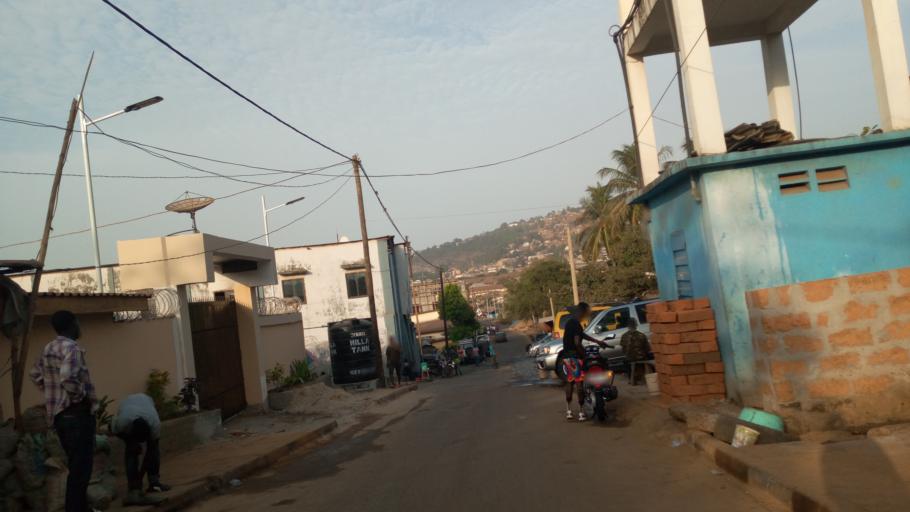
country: SL
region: Western Area
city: Freetown
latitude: 8.4721
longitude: -13.2426
